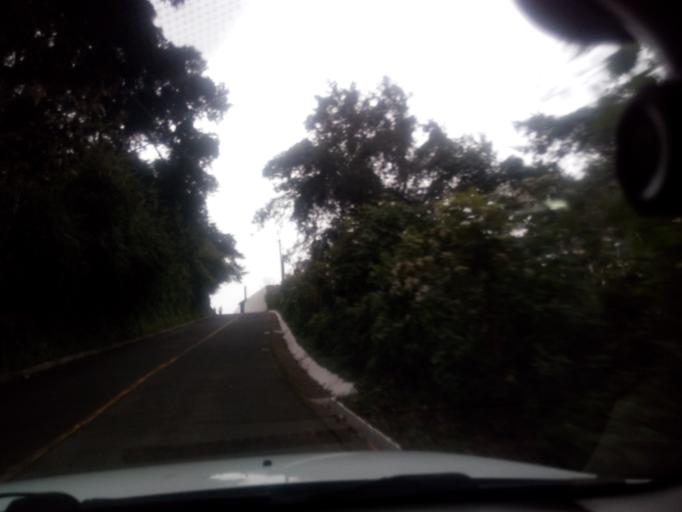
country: GT
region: Sacatepequez
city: San Bartolome Milpas Altas
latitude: 14.5959
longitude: -90.6864
